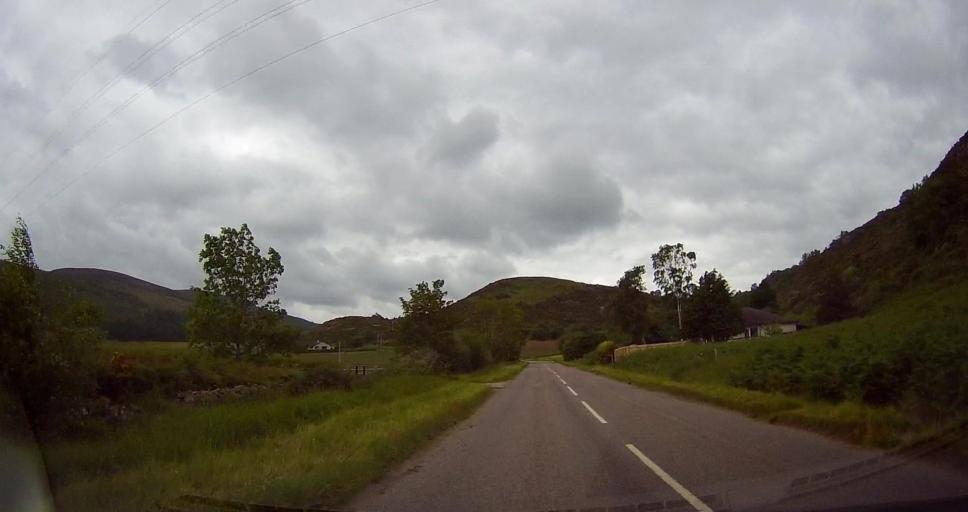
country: GB
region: Scotland
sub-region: Highland
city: Dornoch
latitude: 57.9833
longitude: -4.1305
